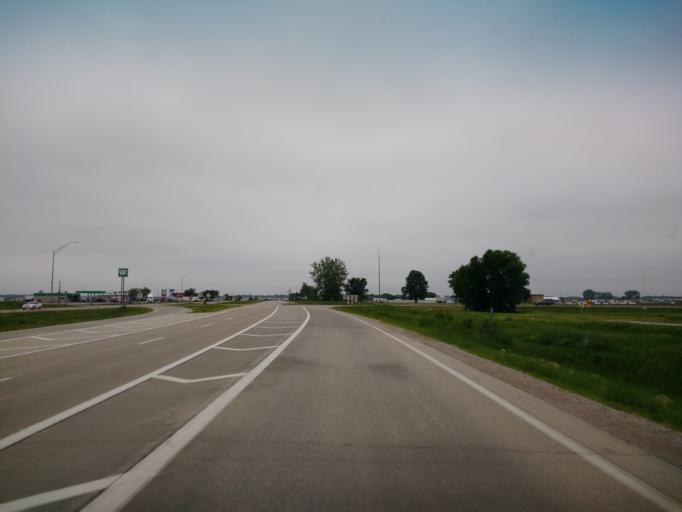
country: US
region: Iowa
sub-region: Clay County
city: Spencer
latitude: 43.1854
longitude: -95.1508
